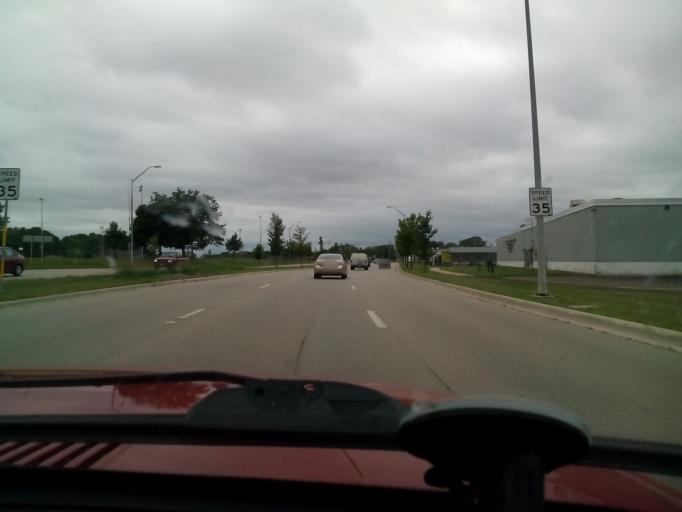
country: US
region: Wisconsin
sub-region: Dane County
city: Maple Bluff
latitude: 43.1062
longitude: -89.3553
